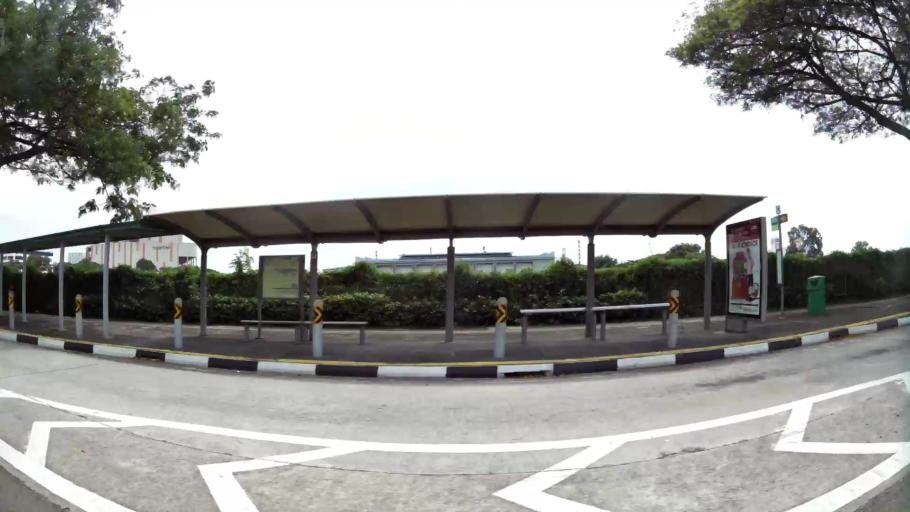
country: MY
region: Johor
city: Johor Bahru
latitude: 1.3225
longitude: 103.6856
